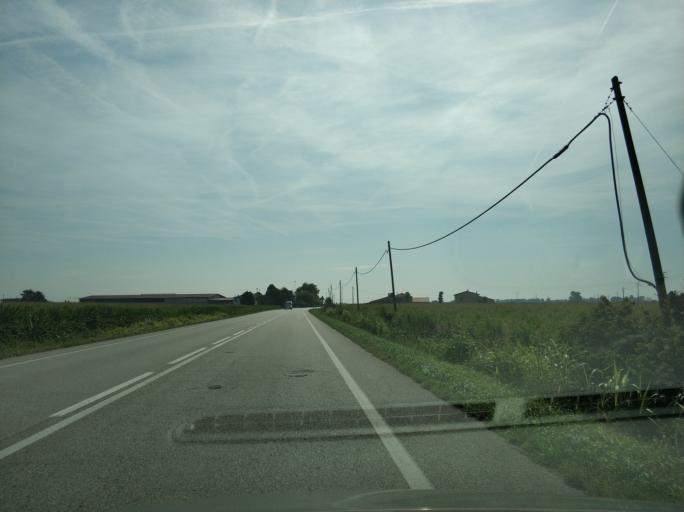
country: IT
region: Veneto
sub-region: Provincia di Padova
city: Correzzola
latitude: 45.2177
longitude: 12.0923
